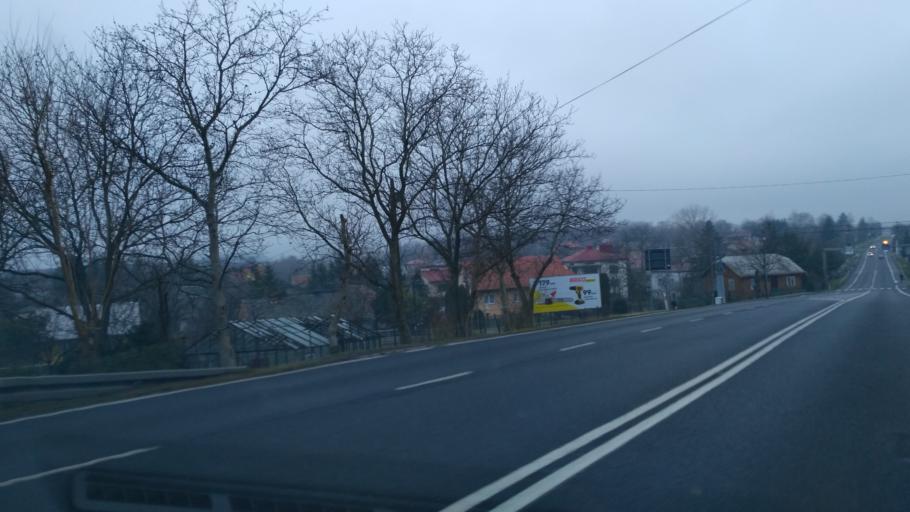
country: PL
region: Subcarpathian Voivodeship
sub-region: Powiat przeworski
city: Mirocin
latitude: 50.0414
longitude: 22.5581
